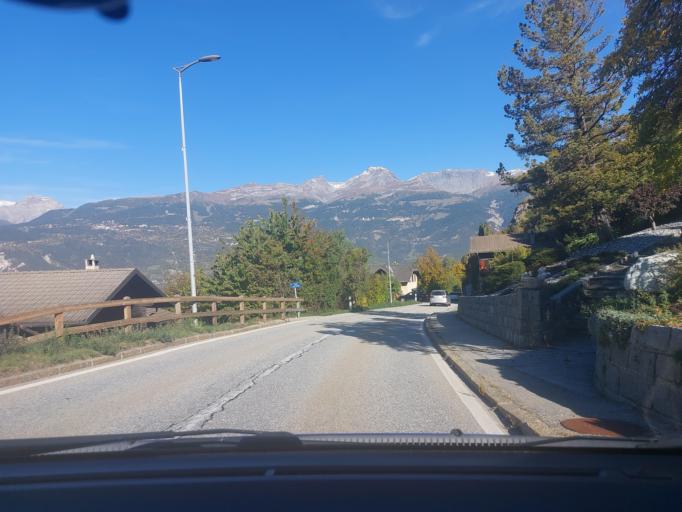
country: CH
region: Valais
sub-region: Sierre District
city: Chippis
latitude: 46.2706
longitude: 7.5518
